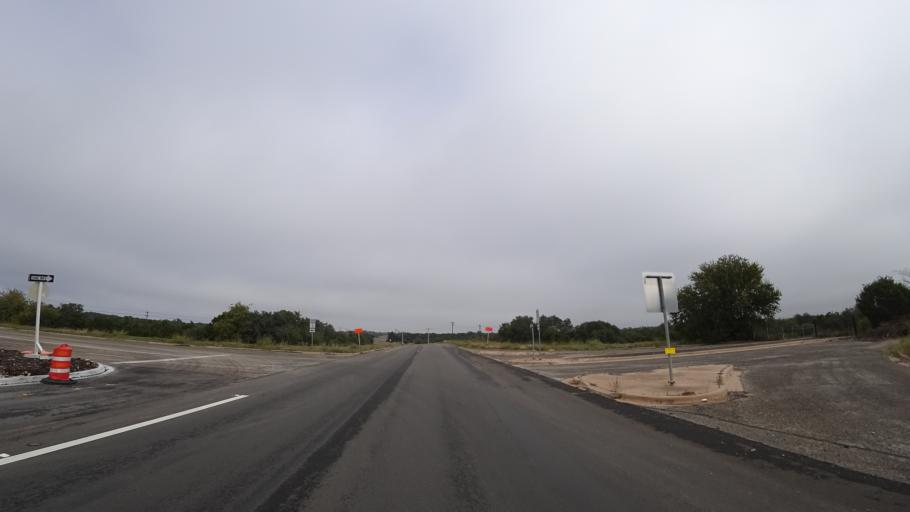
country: US
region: Texas
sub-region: Travis County
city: Shady Hollow
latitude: 30.1801
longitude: -97.8813
